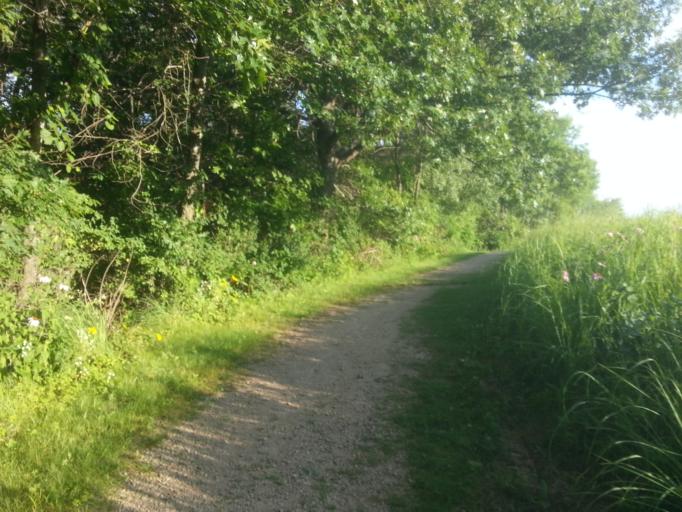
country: US
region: Wisconsin
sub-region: Dane County
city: Middleton
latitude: 43.0730
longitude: -89.4831
